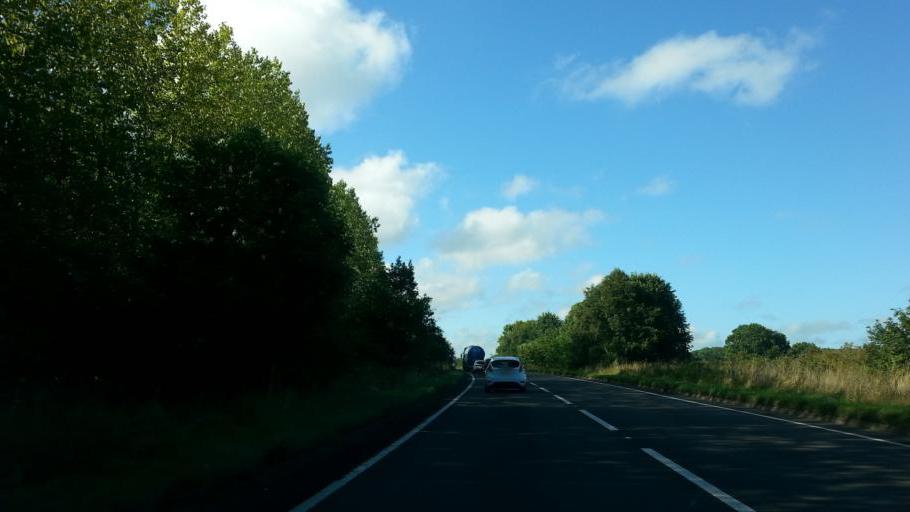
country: GB
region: England
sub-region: District of Rutland
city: South Luffenham
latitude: 52.5689
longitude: -0.5713
